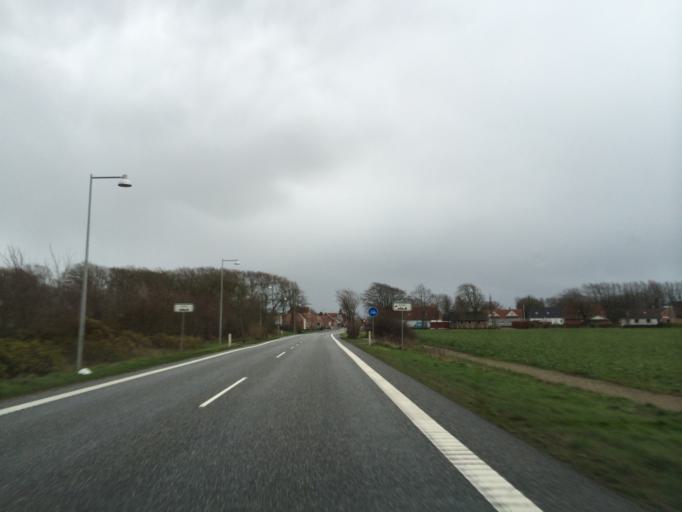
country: DK
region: Central Jutland
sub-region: Ringkobing-Skjern Kommune
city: Tarm
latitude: 55.8046
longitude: 8.4924
